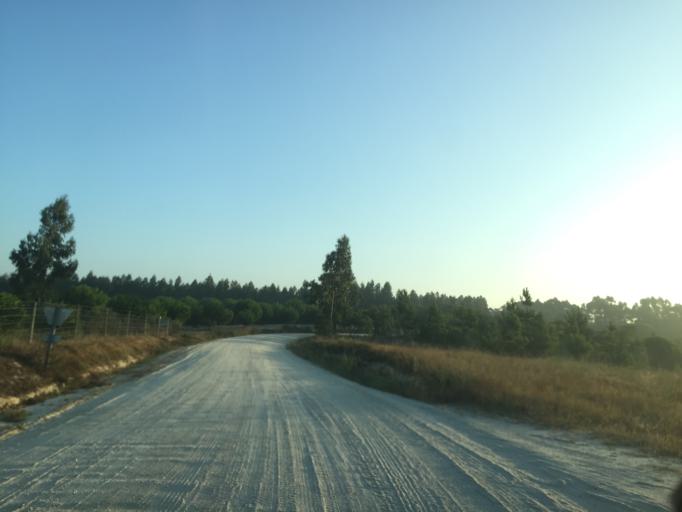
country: PT
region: Santarem
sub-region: Coruche
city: Coruche
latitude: 39.0620
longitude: -8.4077
